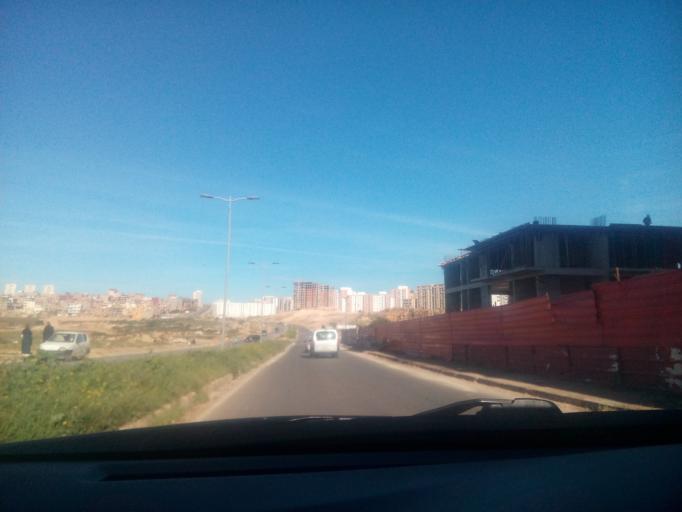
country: DZ
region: Oran
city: Bir el Djir
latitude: 35.7374
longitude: -0.5459
